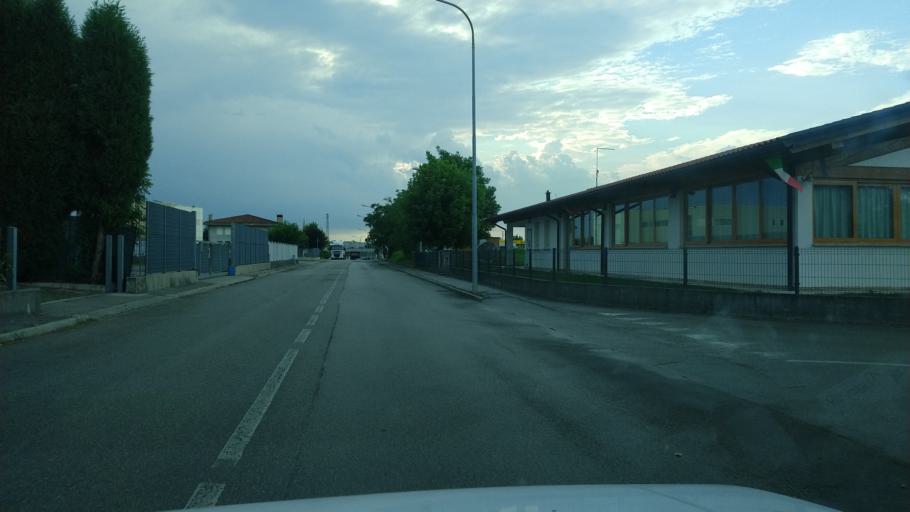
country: IT
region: Veneto
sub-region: Provincia di Vicenza
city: Nove
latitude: 45.7109
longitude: 11.6731
